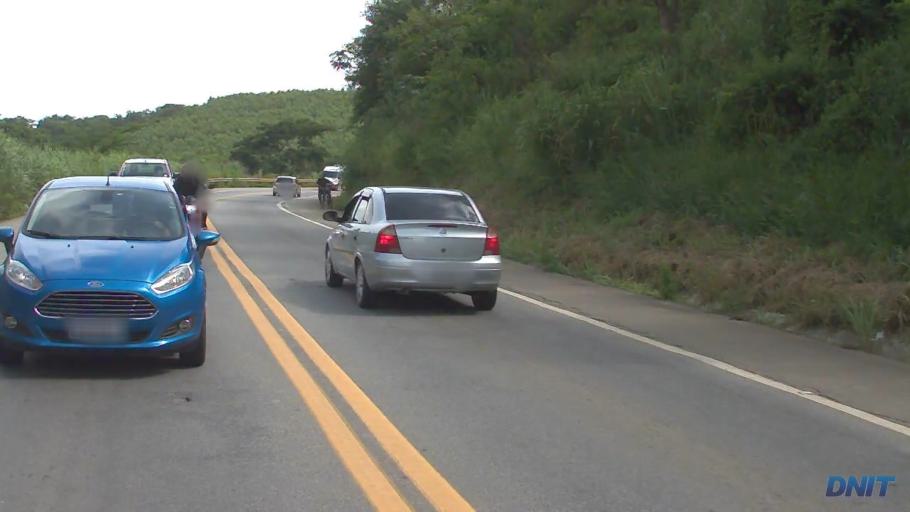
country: BR
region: Minas Gerais
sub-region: Ipaba
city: Ipaba
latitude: -19.3602
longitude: -42.4457
